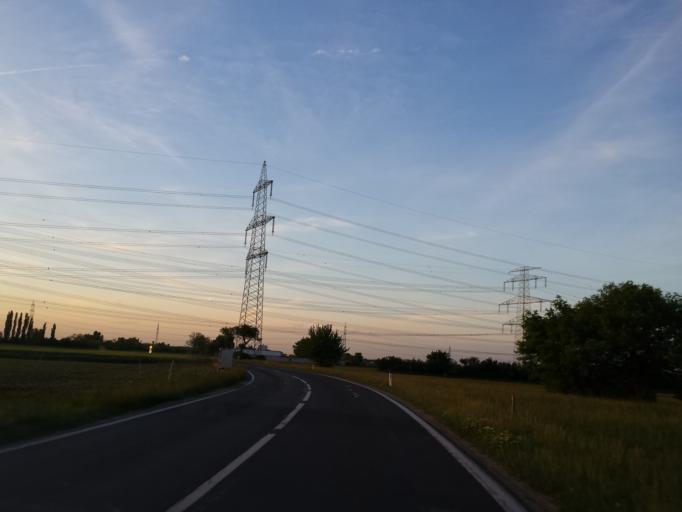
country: AT
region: Lower Austria
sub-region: Politischer Bezirk Tulln
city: Atzenbrugg
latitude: 48.3259
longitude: 15.9084
